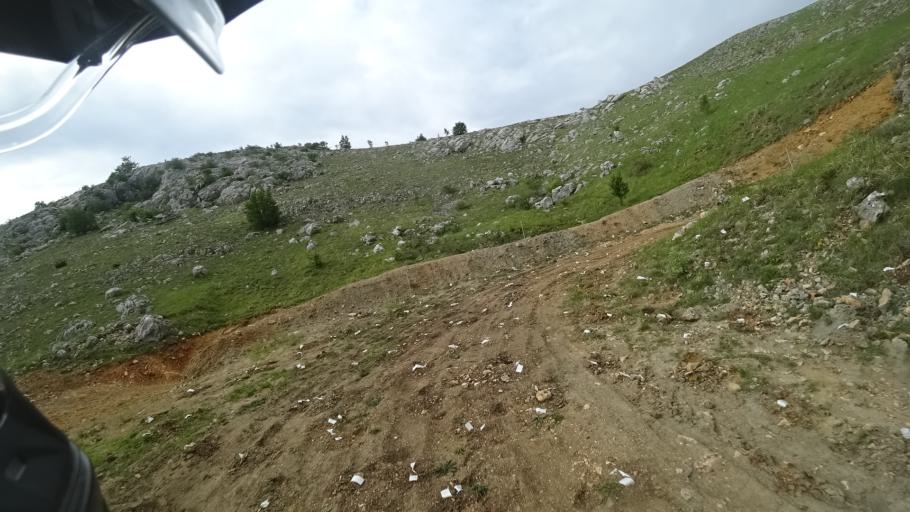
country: HR
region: Sibensko-Kniniska
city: Drnis
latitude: 43.8601
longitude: 16.3774
